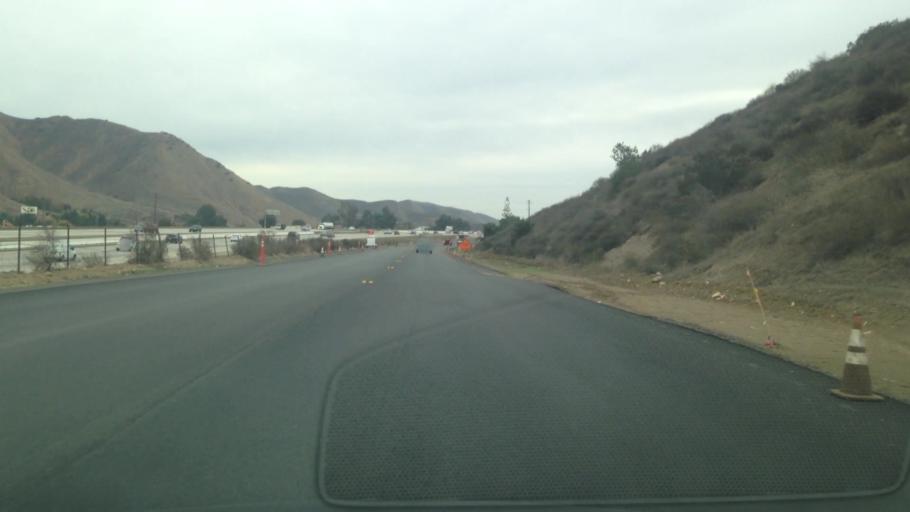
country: US
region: California
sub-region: Riverside County
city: El Cerrito
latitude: 33.7418
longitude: -117.4371
